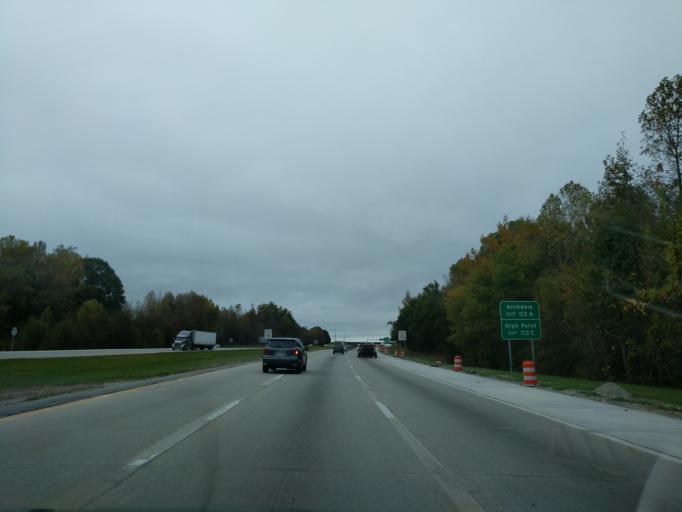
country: US
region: North Carolina
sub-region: Randolph County
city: Archdale
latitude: 35.9176
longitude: -79.9443
